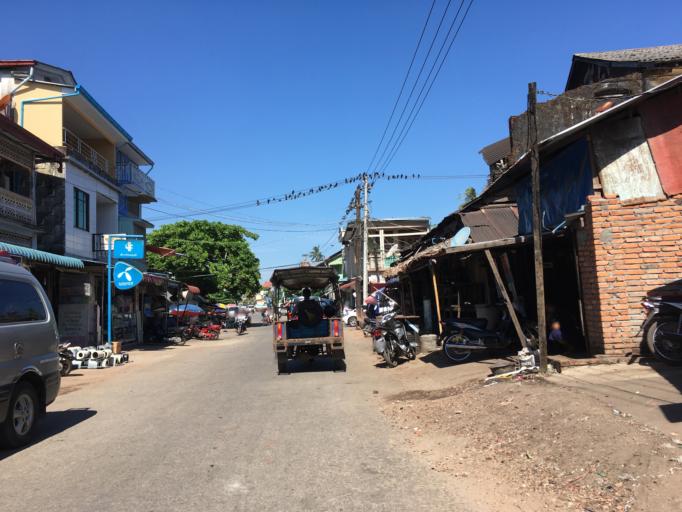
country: MM
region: Mon
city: Mawlamyine
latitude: 16.4554
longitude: 97.6277
